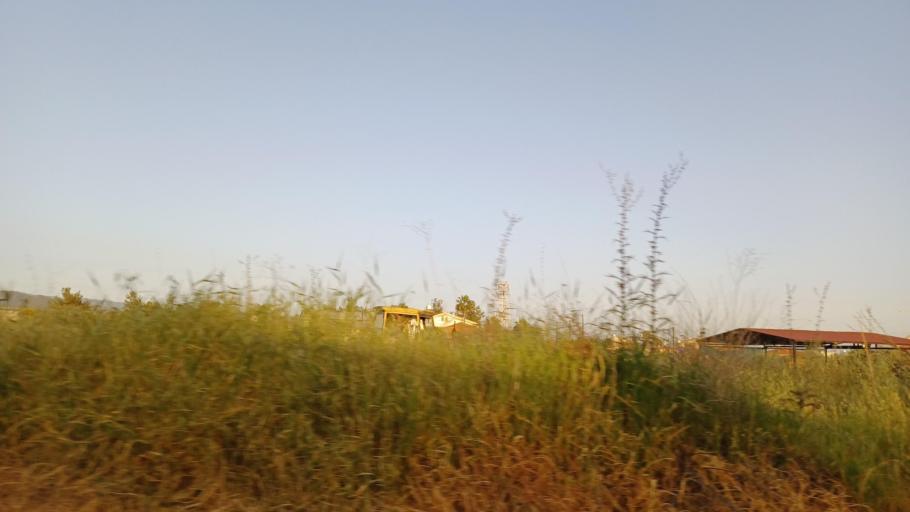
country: CY
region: Lefkosia
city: Astromeritis
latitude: 35.0800
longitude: 33.0160
